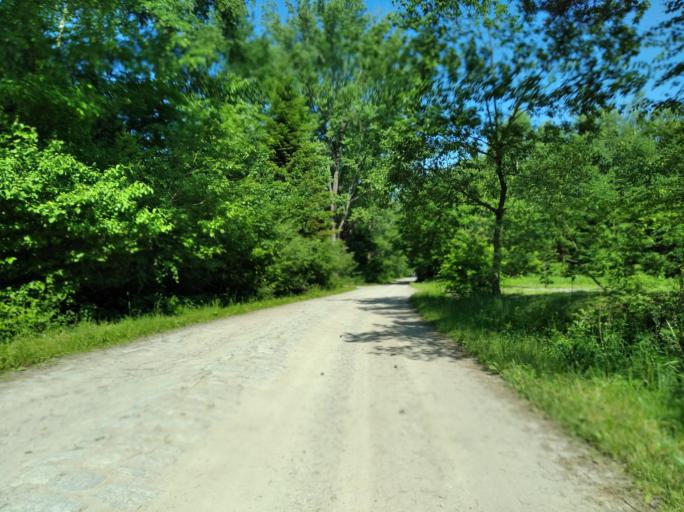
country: PL
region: Subcarpathian Voivodeship
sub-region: Powiat krosnienski
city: Odrzykon
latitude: 49.7699
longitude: 21.7694
